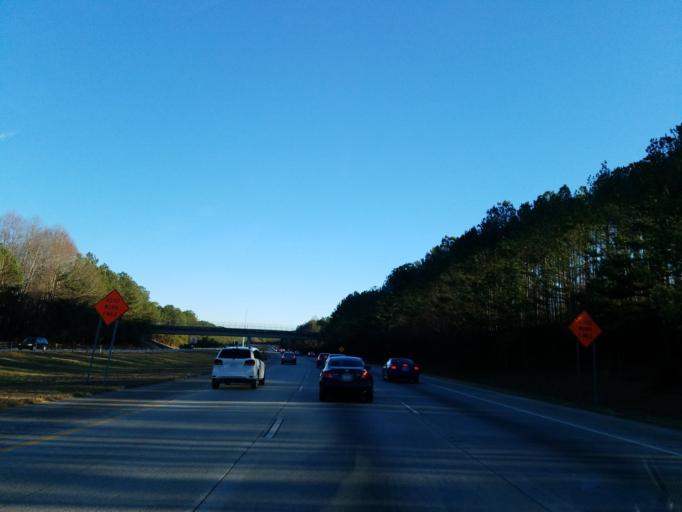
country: US
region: Georgia
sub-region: Clayton County
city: Lake City
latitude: 33.6007
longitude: -84.2928
